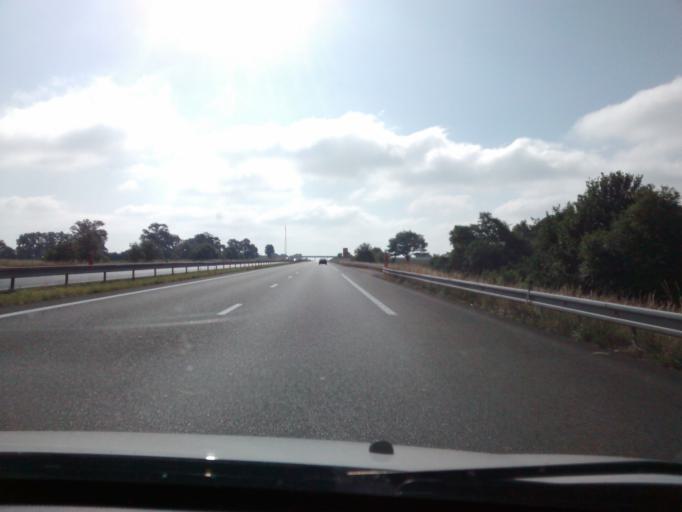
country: FR
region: Pays de la Loire
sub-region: Departement de la Mayenne
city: Soulge-sur-Ouette
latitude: 48.0708
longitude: -0.5685
